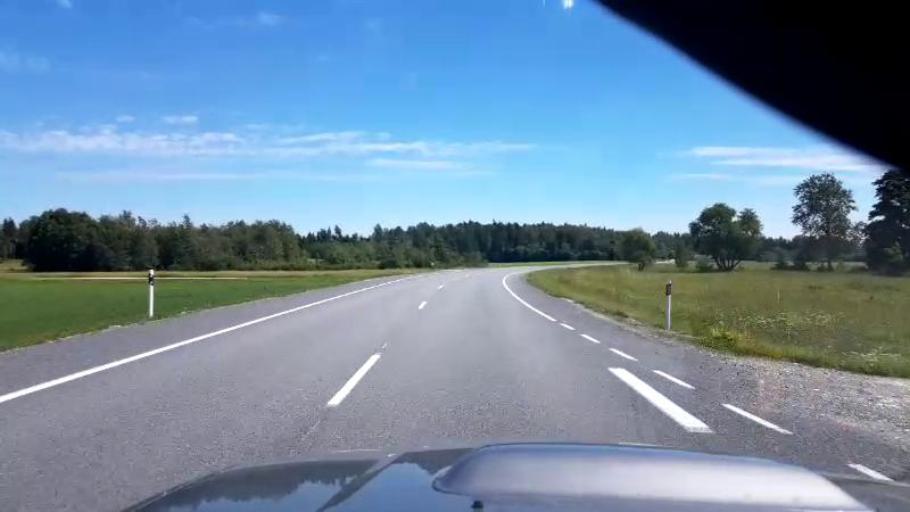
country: EE
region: Jaervamaa
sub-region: Jaerva-Jaani vald
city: Jarva-Jaani
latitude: 59.0012
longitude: 25.9359
